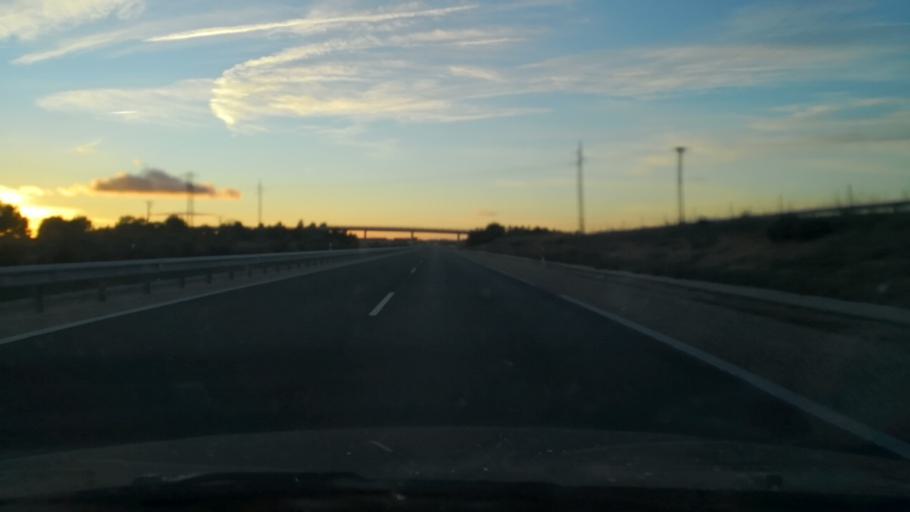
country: ES
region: Castille and Leon
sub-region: Provincia de Valladolid
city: Torrecilla de la Abadesa
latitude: 41.5059
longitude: -5.0625
